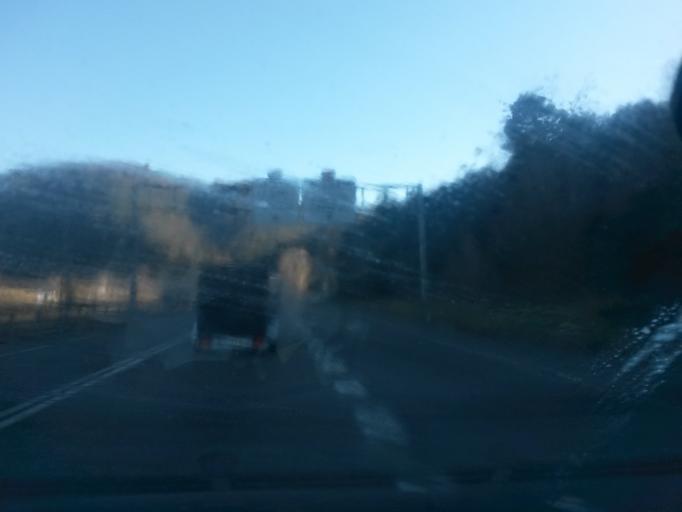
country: ES
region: Catalonia
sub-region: Provincia de Girona
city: Sant Julia de Ramis
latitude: 42.0245
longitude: 2.8485
